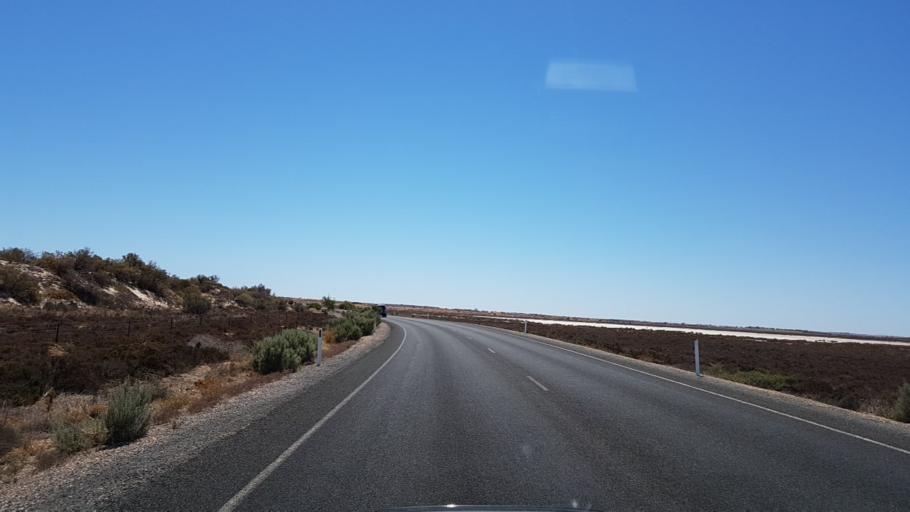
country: AU
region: South Australia
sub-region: Copper Coast
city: Wallaroo
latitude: -33.9200
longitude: 137.6448
